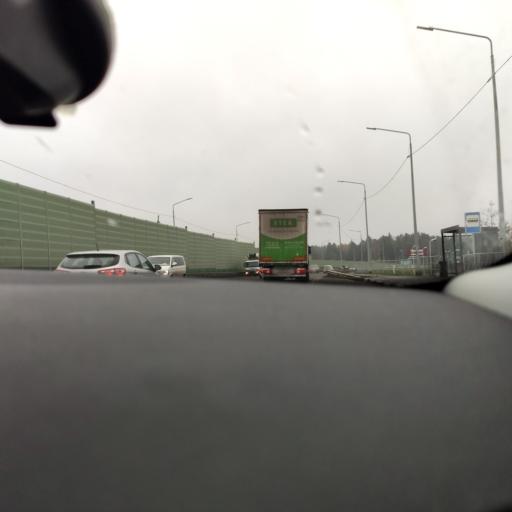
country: RU
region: Moskovskaya
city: Pavlovskaya Sloboda
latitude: 55.8101
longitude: 37.1302
